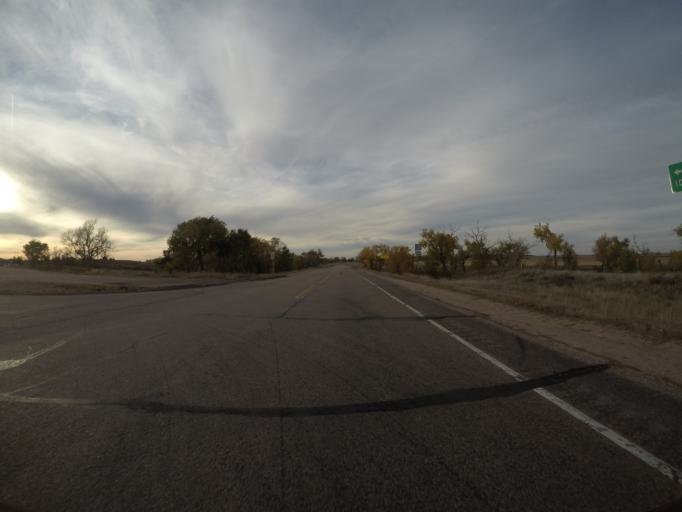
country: US
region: Colorado
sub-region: Yuma County
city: Yuma
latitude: 39.6565
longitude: -102.8445
